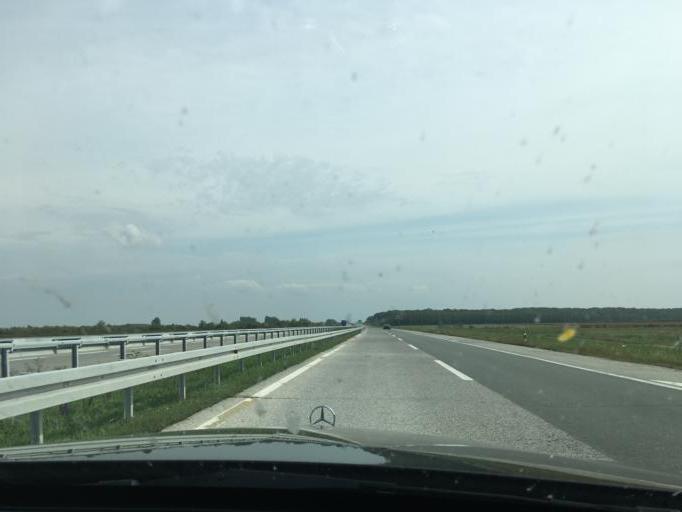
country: RS
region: Autonomna Pokrajina Vojvodina
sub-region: Sremski Okrug
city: Sid
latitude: 45.0449
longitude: 19.1615
